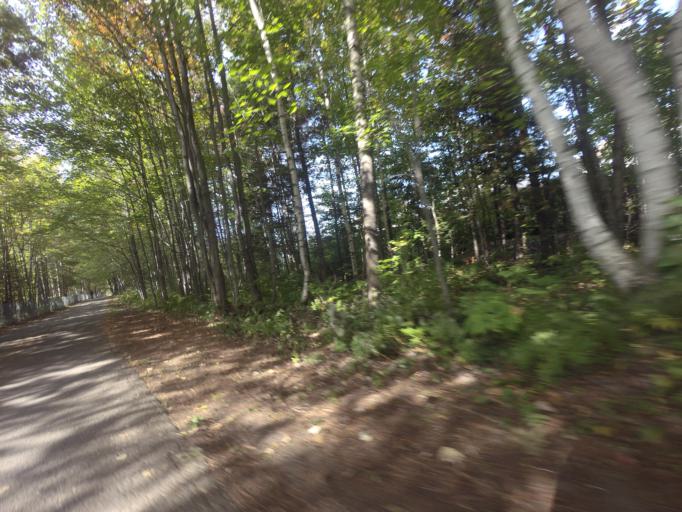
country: CA
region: Quebec
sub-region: Laurentides
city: Blainville
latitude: 45.7046
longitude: -73.9087
